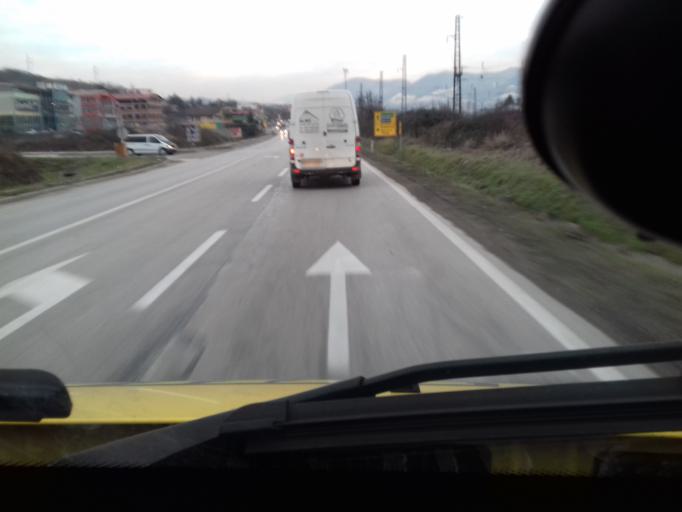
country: BA
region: Federation of Bosnia and Herzegovina
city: Zenica
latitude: 44.2287
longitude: 17.9074
